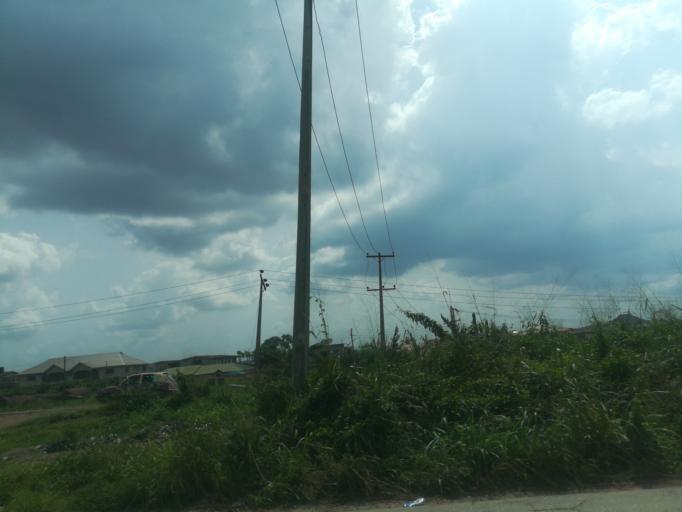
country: NG
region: Oyo
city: Ibadan
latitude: 7.4376
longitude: 3.9309
